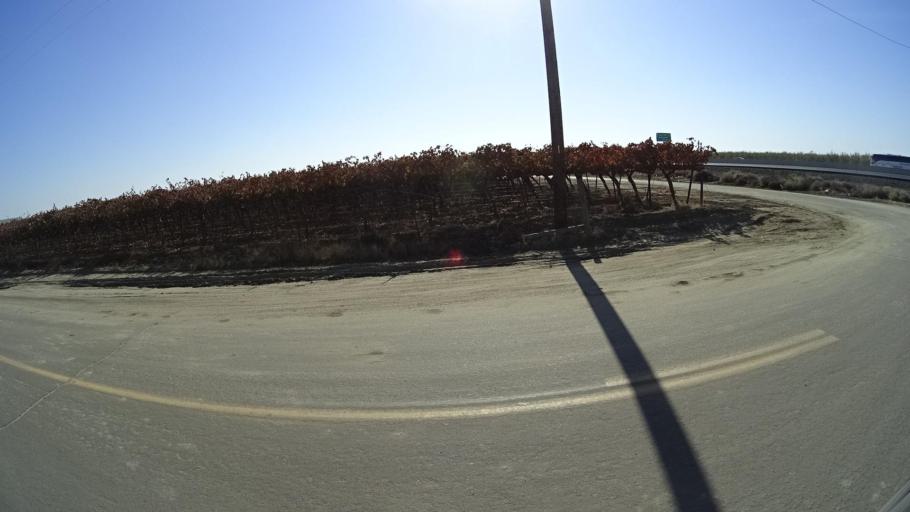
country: US
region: California
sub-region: Kern County
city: McFarland
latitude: 35.7039
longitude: -119.2320
